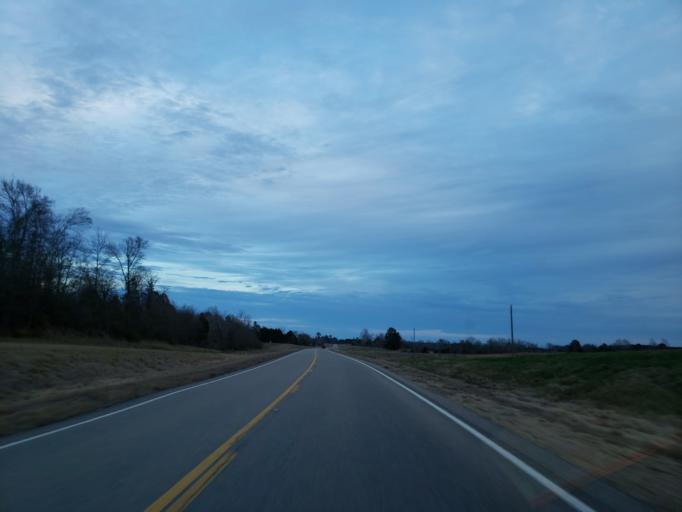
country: US
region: Mississippi
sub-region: Kemper County
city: De Kalb
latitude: 32.8306
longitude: -88.3846
